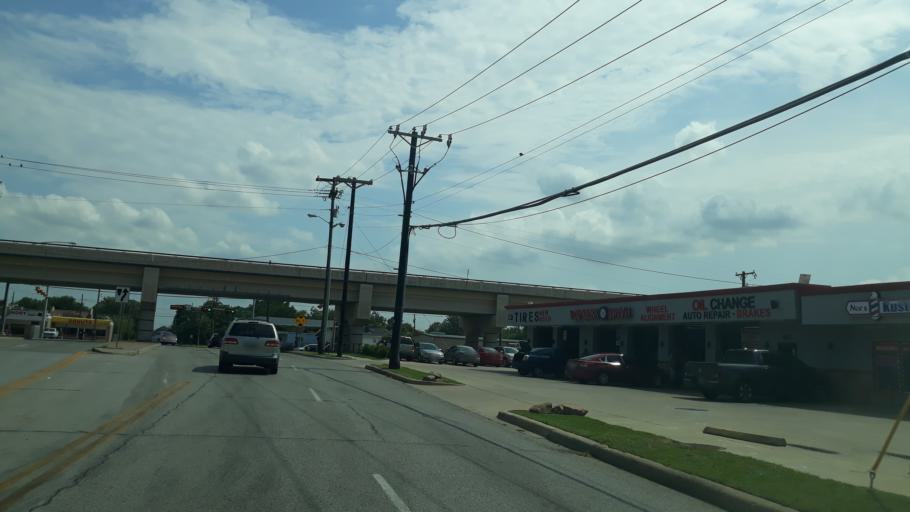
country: US
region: Texas
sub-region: Dallas County
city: Irving
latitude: 32.8162
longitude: -96.9765
